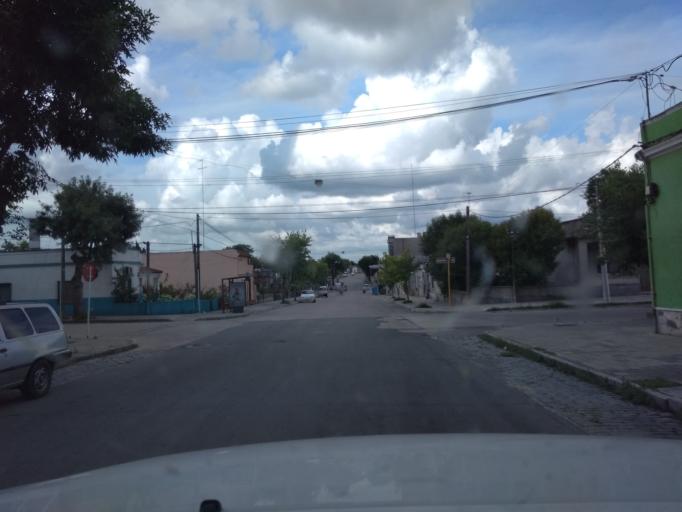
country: UY
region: Florida
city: Florida
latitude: -34.0921
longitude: -56.2173
